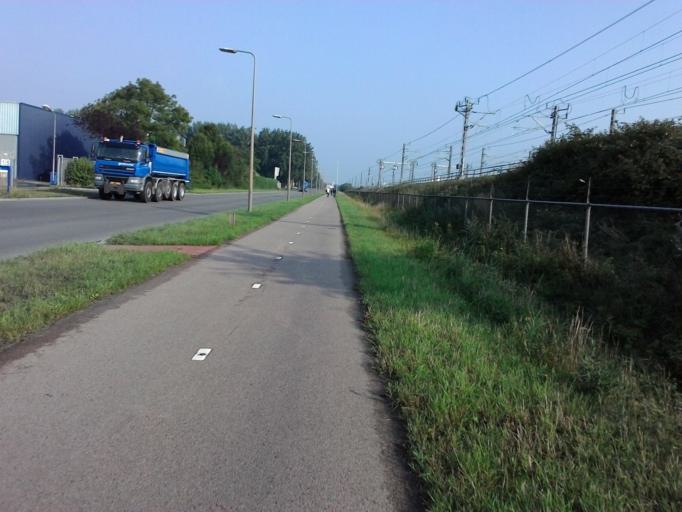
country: NL
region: Utrecht
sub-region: Stichtse Vecht
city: Maarssen
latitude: 52.1167
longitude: 5.0654
